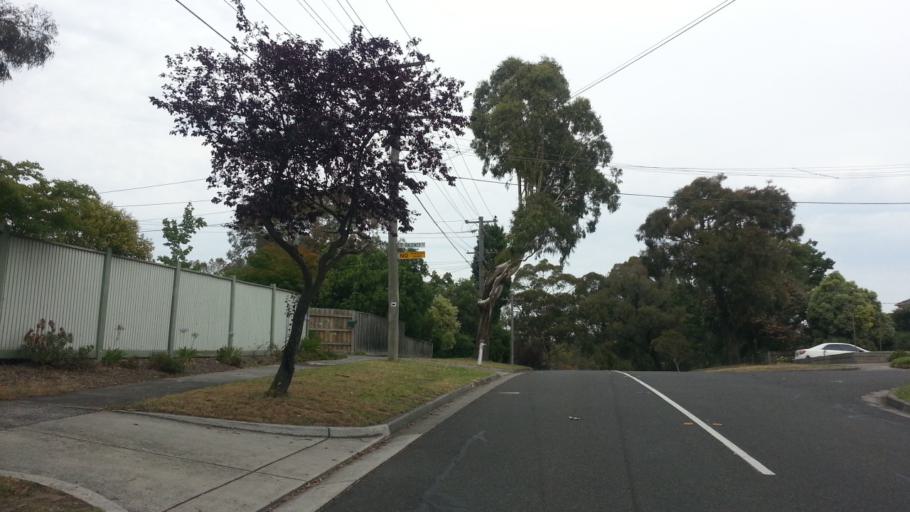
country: AU
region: Victoria
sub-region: Whitehorse
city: Vermont
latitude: -37.8300
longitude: 145.2030
